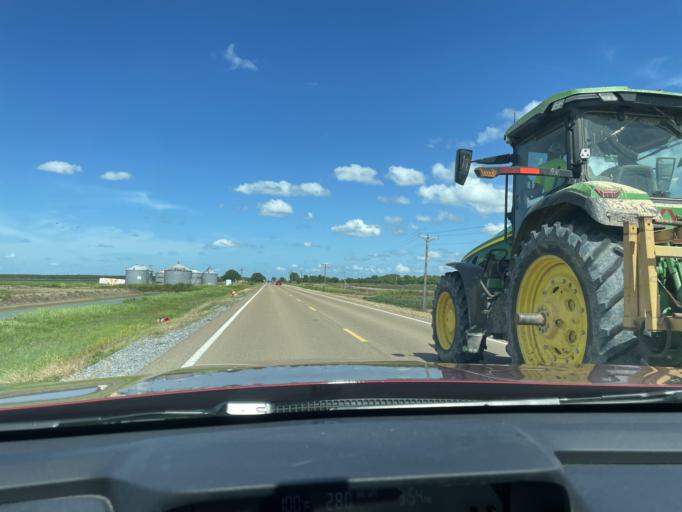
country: US
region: Mississippi
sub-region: Humphreys County
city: Belzoni
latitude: 33.1830
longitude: -90.6524
